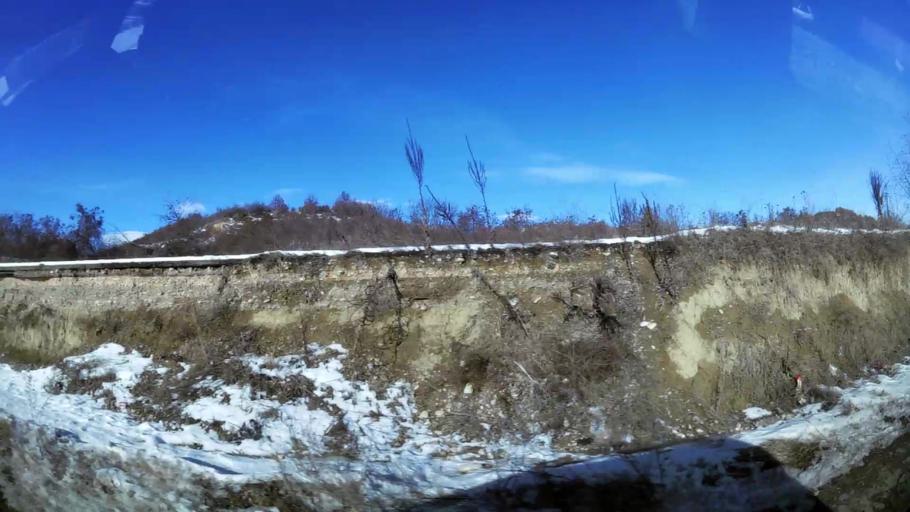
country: MK
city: Ljubin
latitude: 41.9871
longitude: 21.3081
